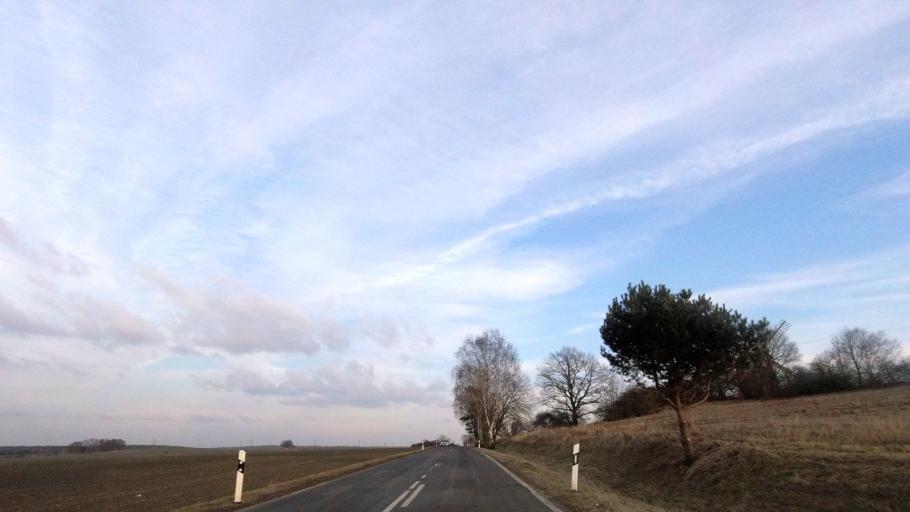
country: DE
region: Brandenburg
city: Belzig
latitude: 52.1075
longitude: 12.5378
